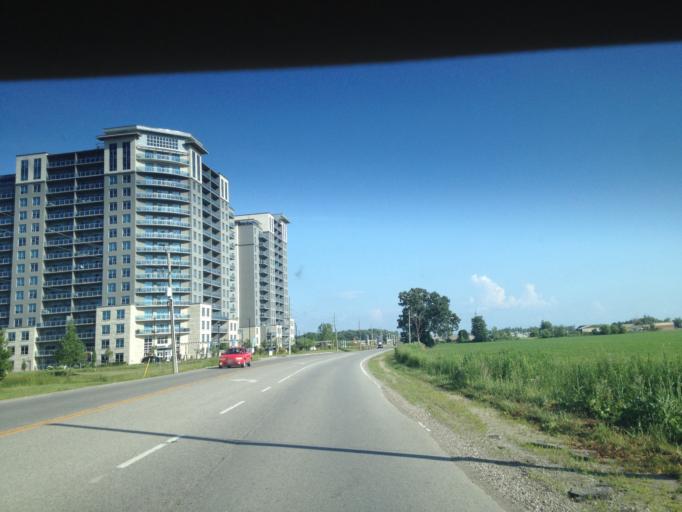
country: CA
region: Ontario
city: London
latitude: 43.0156
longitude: -81.3411
